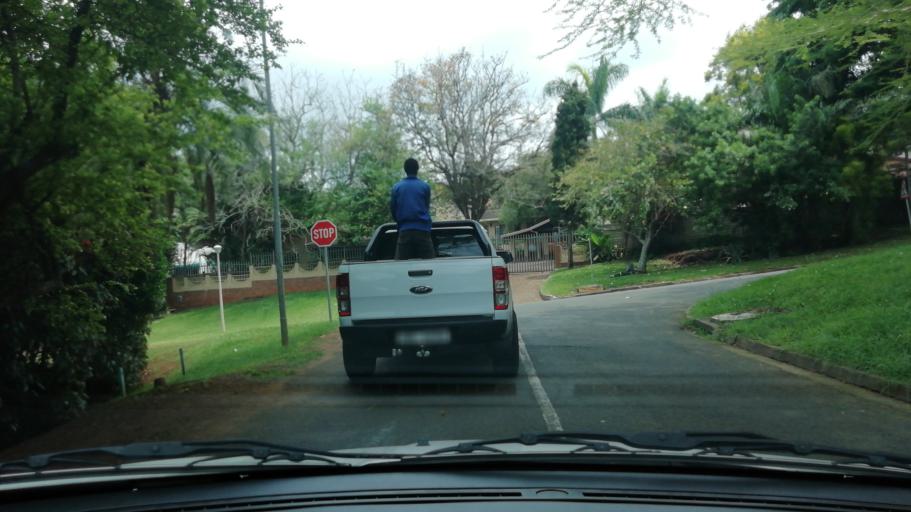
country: ZA
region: KwaZulu-Natal
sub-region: uThungulu District Municipality
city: Empangeni
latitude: -28.7522
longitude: 31.8876
